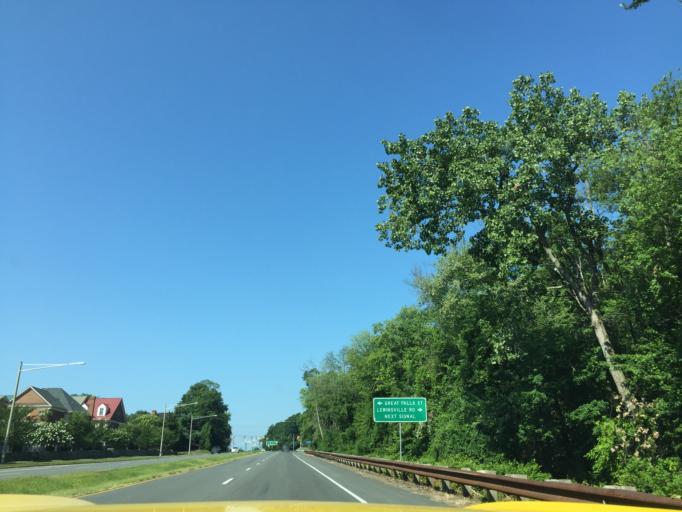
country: US
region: Virginia
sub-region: Fairfax County
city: McLean
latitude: 38.9329
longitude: -77.1957
